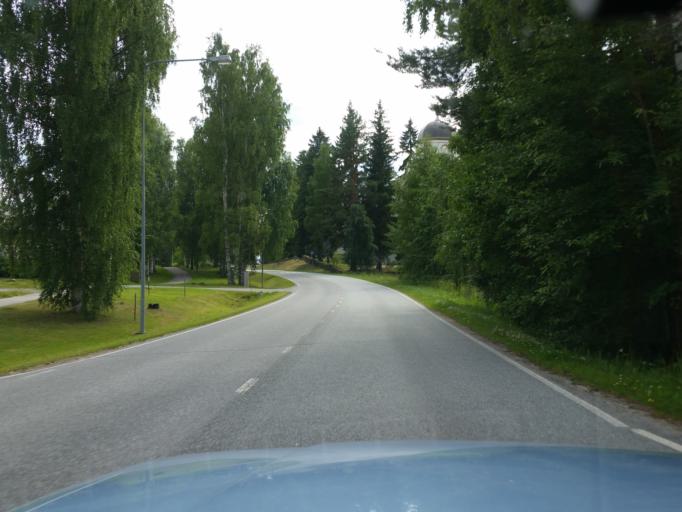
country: FI
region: Southern Savonia
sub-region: Savonlinna
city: Sulkava
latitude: 61.7907
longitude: 28.3755
